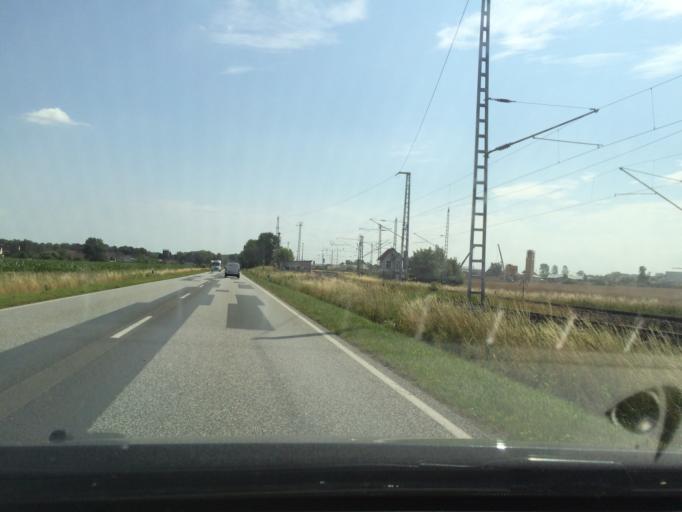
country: DE
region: Mecklenburg-Vorpommern
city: Samtens
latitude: 54.3546
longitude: 13.2797
